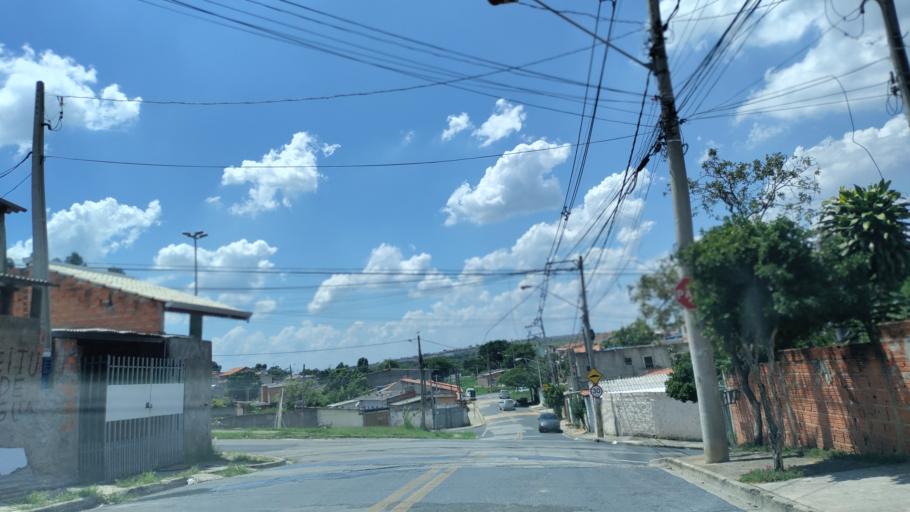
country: BR
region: Sao Paulo
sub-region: Sorocaba
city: Sorocaba
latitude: -23.4693
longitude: -47.4666
